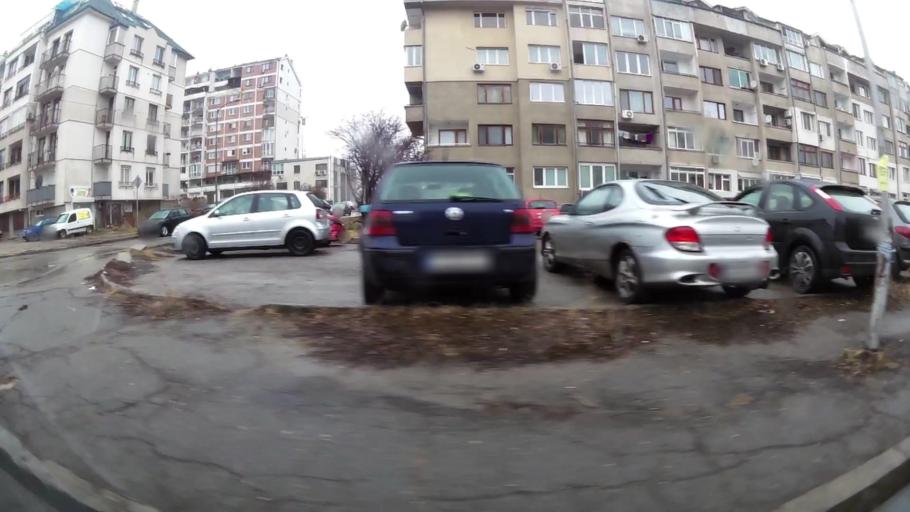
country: BG
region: Sofia-Capital
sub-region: Stolichna Obshtina
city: Sofia
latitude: 42.6376
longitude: 23.3763
